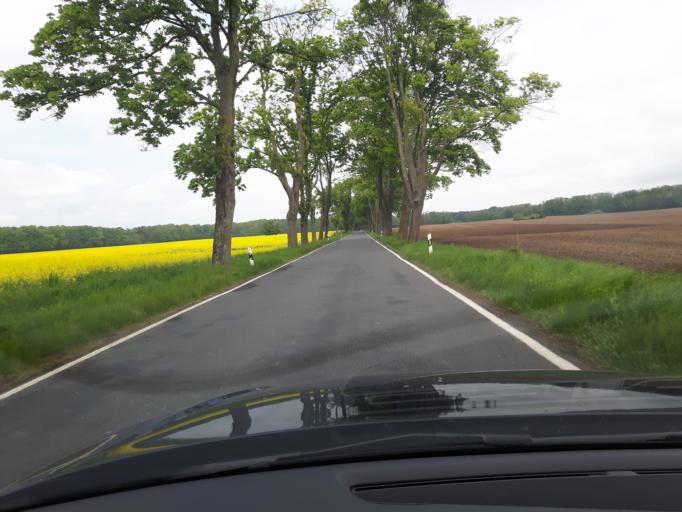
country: DE
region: Mecklenburg-Vorpommern
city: Velgast
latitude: 54.2199
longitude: 12.7347
